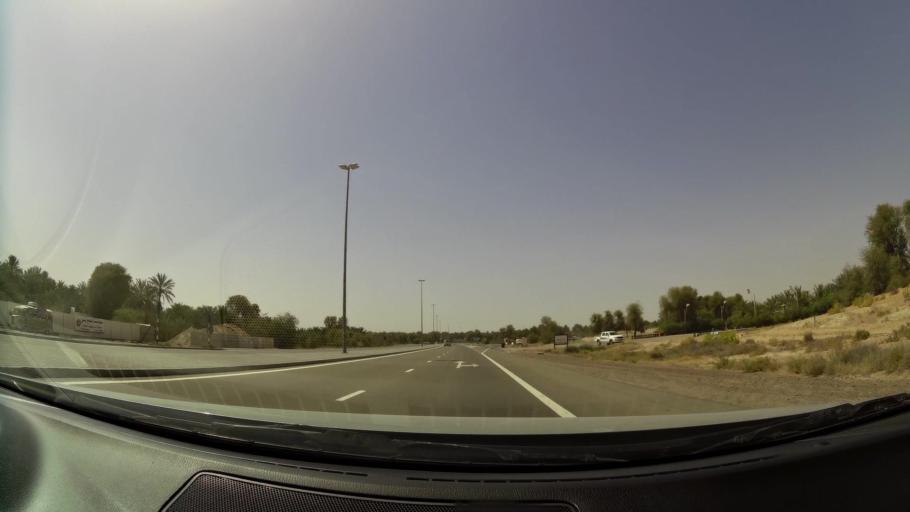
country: OM
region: Al Buraimi
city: Al Buraymi
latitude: 24.2997
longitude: 55.7654
